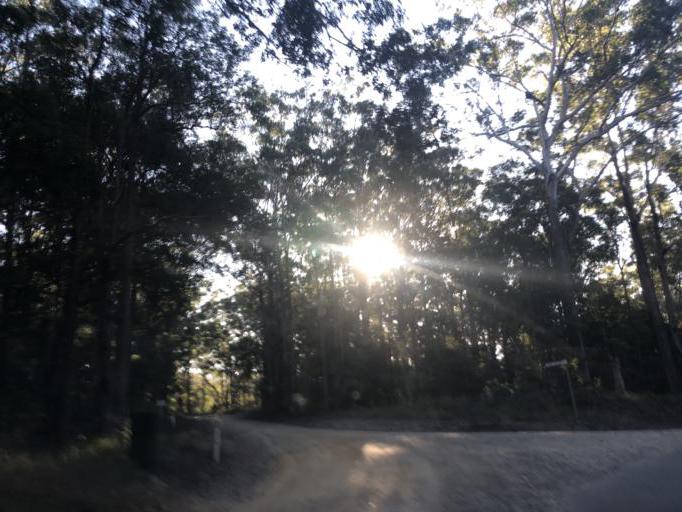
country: AU
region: New South Wales
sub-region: Nambucca Shire
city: Nambucca
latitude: -30.6094
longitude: 152.9746
